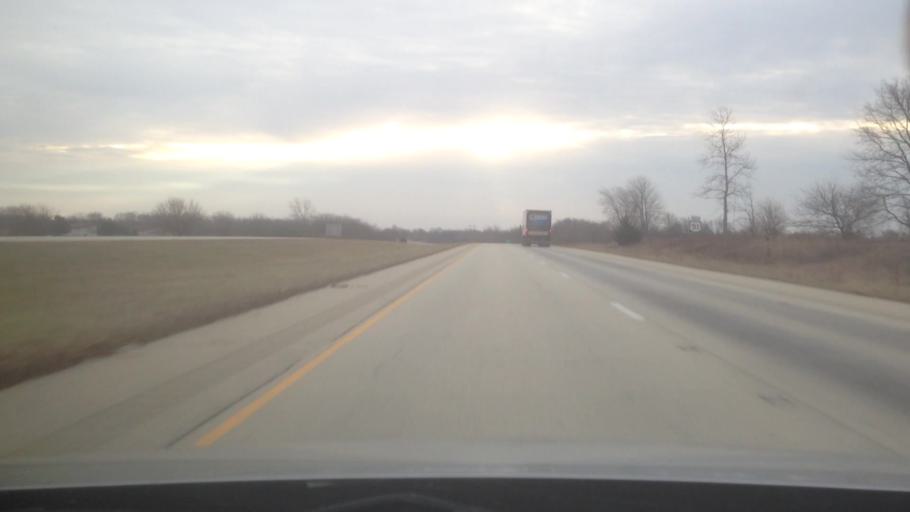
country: US
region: Illinois
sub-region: Macon County
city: Decatur
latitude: 39.7944
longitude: -88.9995
